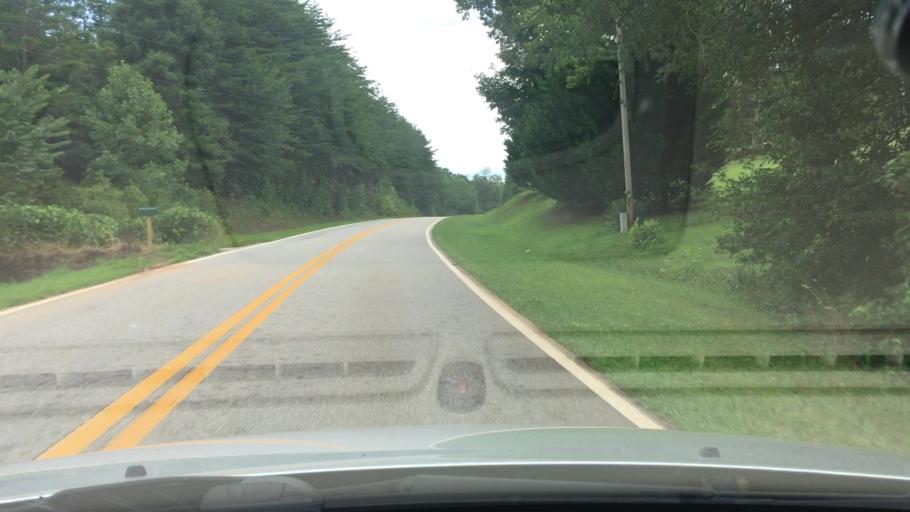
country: US
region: Georgia
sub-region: Lumpkin County
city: Dahlonega
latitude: 34.5924
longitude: -83.8897
